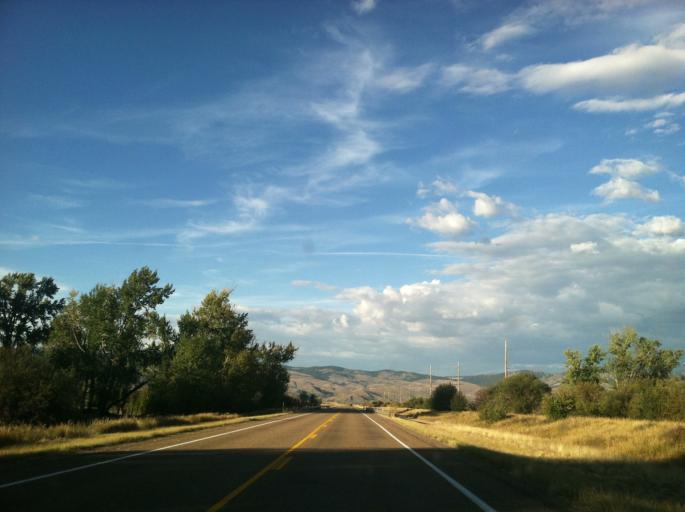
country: US
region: Montana
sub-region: Granite County
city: Philipsburg
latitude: 46.6120
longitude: -113.1787
